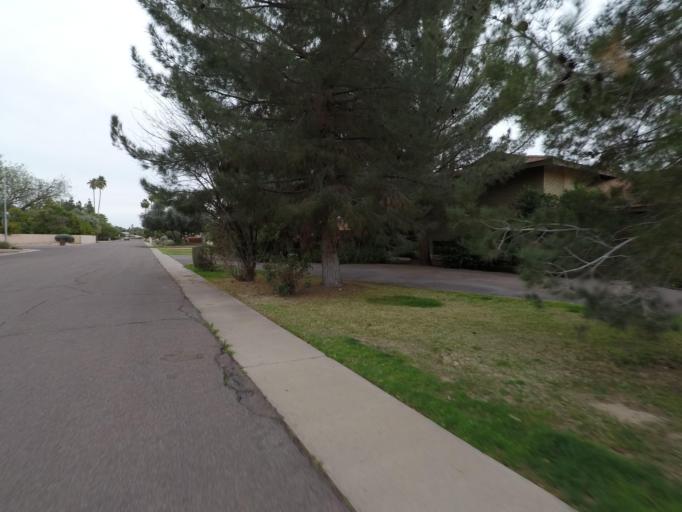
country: US
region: Arizona
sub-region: Maricopa County
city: Guadalupe
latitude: 33.3400
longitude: -111.9272
